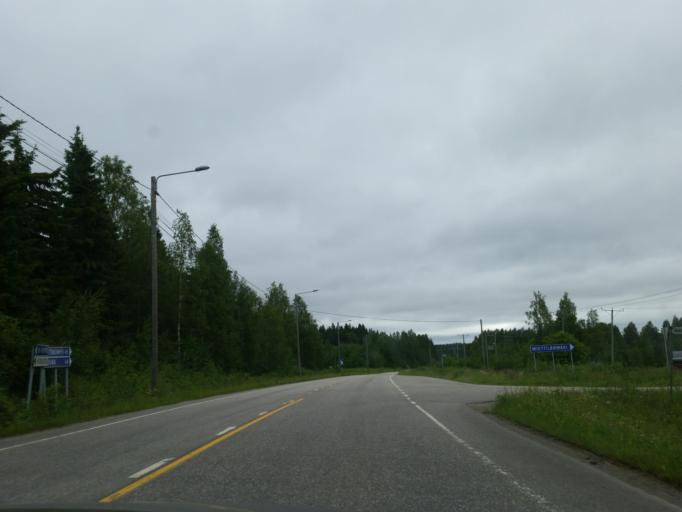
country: FI
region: Northern Savo
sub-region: Koillis-Savo
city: Kaavi
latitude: 62.9738
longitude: 28.5006
